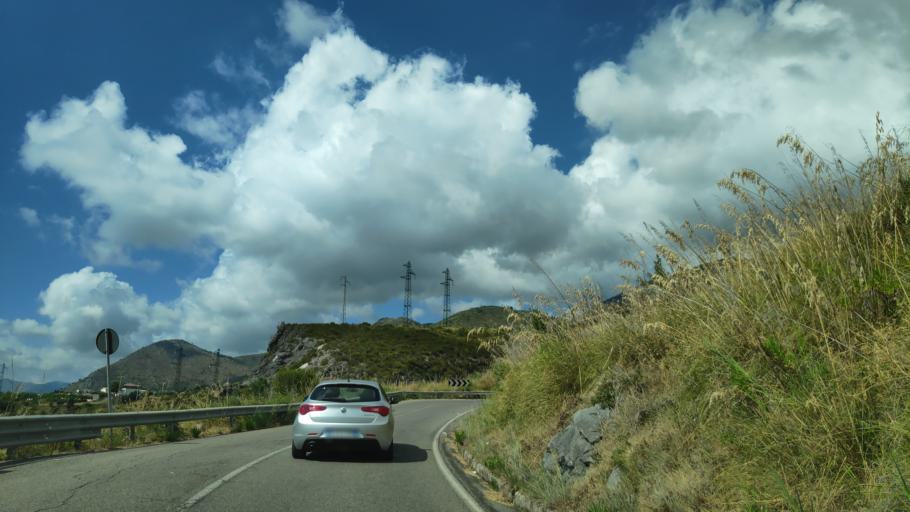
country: IT
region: Calabria
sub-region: Provincia di Cosenza
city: San Nicola Arcella
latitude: 39.8662
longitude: 15.7953
